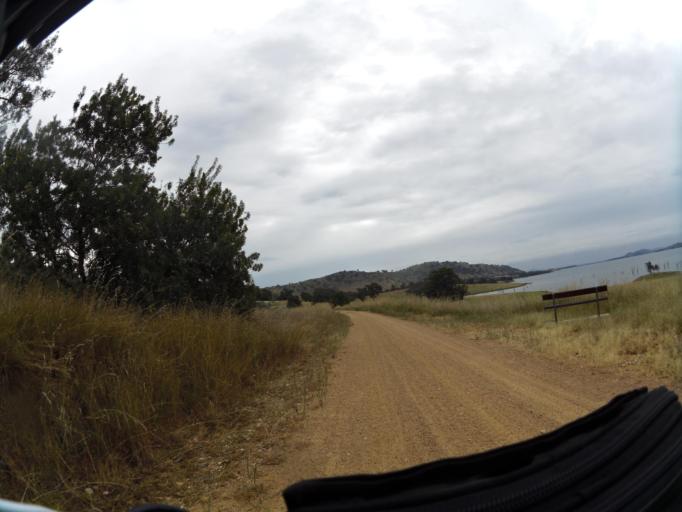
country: AU
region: New South Wales
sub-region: Albury Municipality
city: East Albury
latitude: -36.2027
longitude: 147.0493
